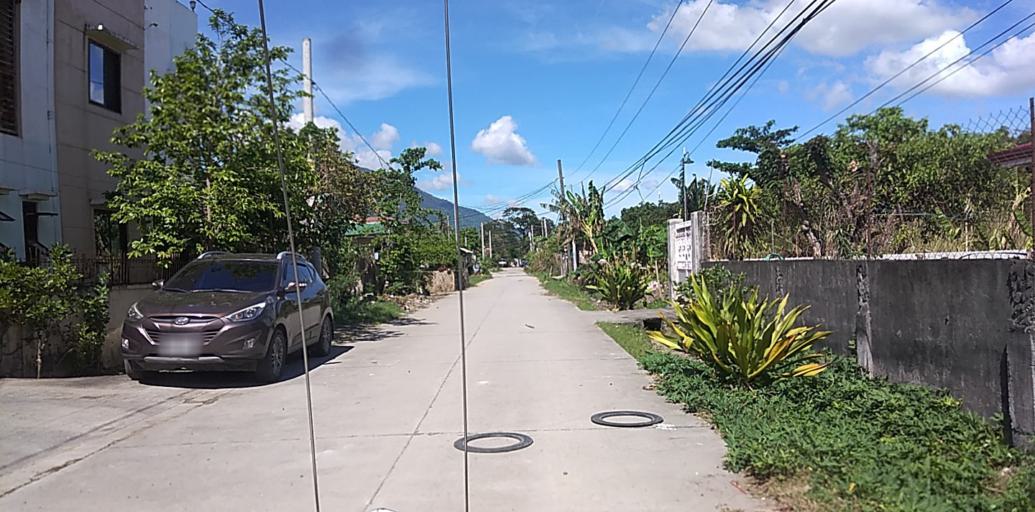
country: PH
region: Central Luzon
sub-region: Province of Pampanga
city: Arayat
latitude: 15.1364
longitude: 120.7749
